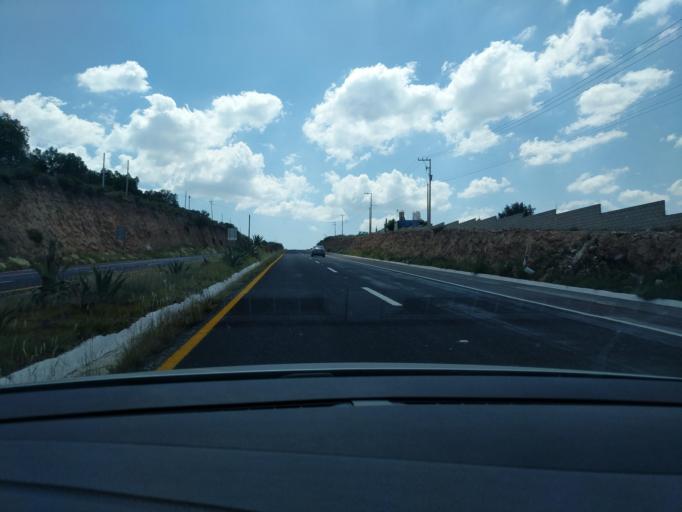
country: MX
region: Hidalgo
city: Zempoala
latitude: 19.8929
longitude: -98.6697
